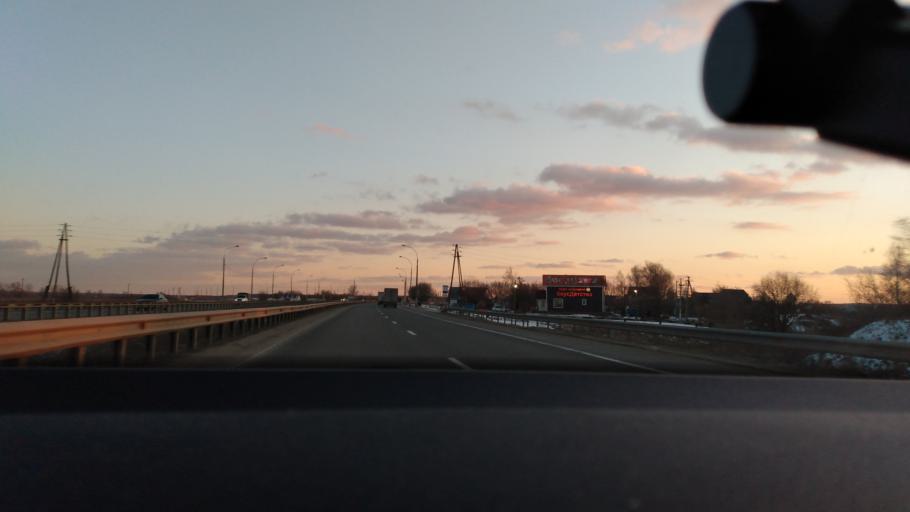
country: RU
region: Moskovskaya
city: Kolomna
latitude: 55.0954
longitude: 38.9034
